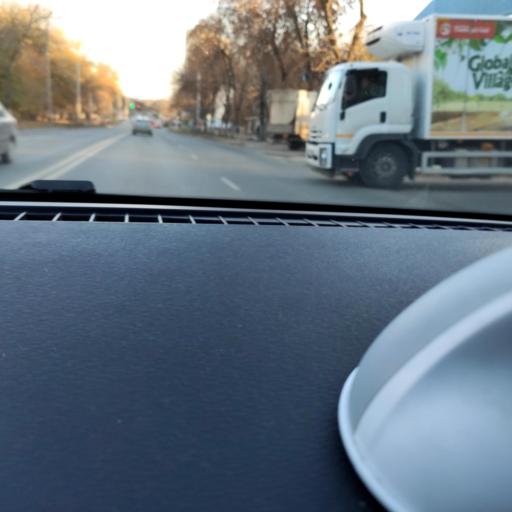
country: RU
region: Samara
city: Samara
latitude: 53.2530
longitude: 50.2348
